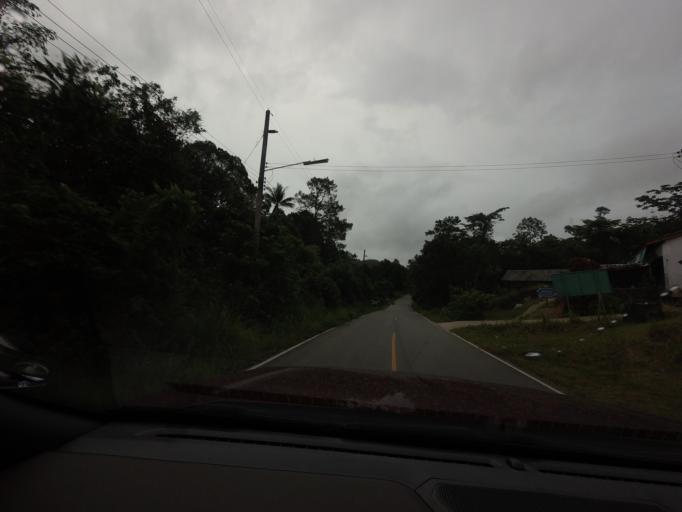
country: TH
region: Narathiwat
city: Chanae
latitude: 6.0297
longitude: 101.6935
